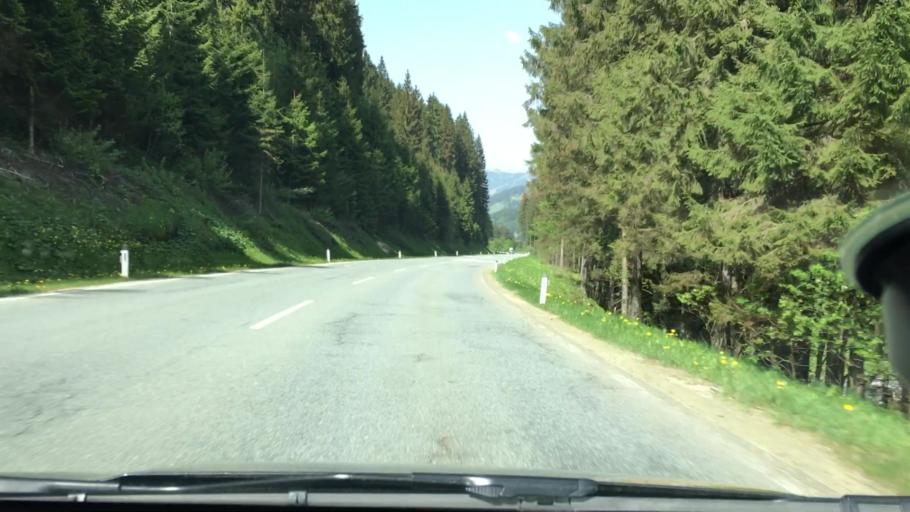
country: AT
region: Tyrol
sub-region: Politischer Bezirk Kitzbuhel
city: Jochberg
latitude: 47.3390
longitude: 12.4076
